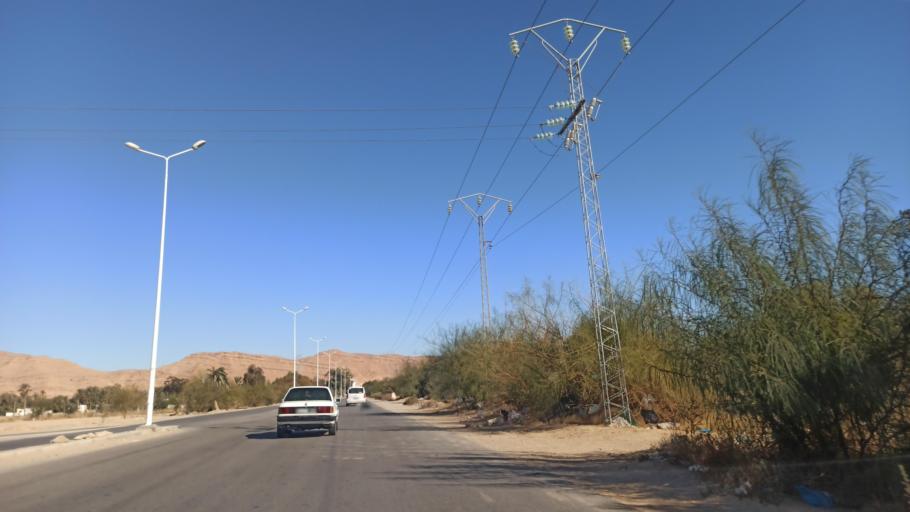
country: TN
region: Gafsa
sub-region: Gafsa Municipality
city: Gafsa
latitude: 34.4162
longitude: 8.7420
